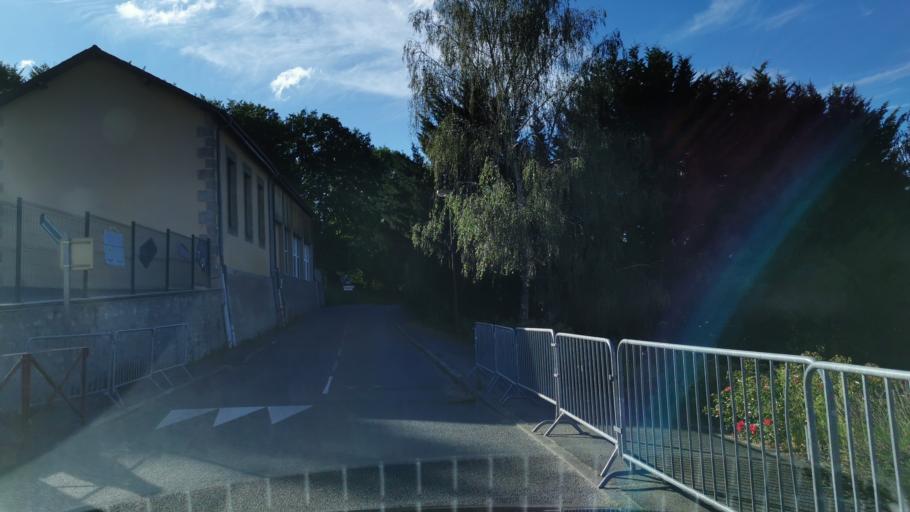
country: FR
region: Bourgogne
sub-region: Departement de Saone-et-Loire
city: Marmagne
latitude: 46.8408
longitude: 4.3285
